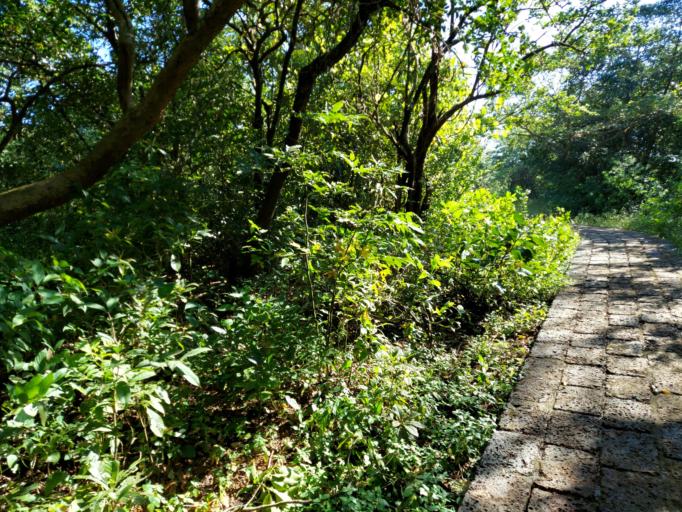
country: IN
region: Maharashtra
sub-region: Sindhudurg
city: Kudal
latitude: 16.0830
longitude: 73.8446
